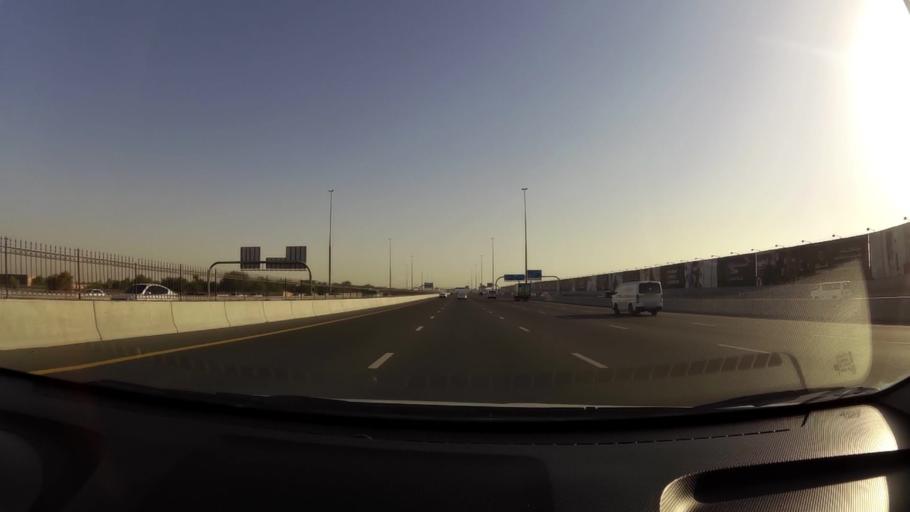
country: AE
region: Ash Shariqah
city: Sharjah
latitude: 25.3306
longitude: 55.4624
